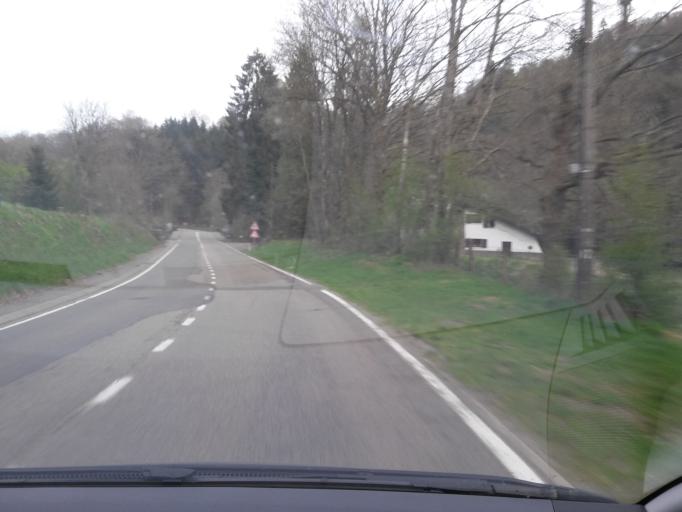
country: BE
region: Wallonia
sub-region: Province du Luxembourg
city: Herbeumont
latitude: 49.7700
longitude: 5.2350
